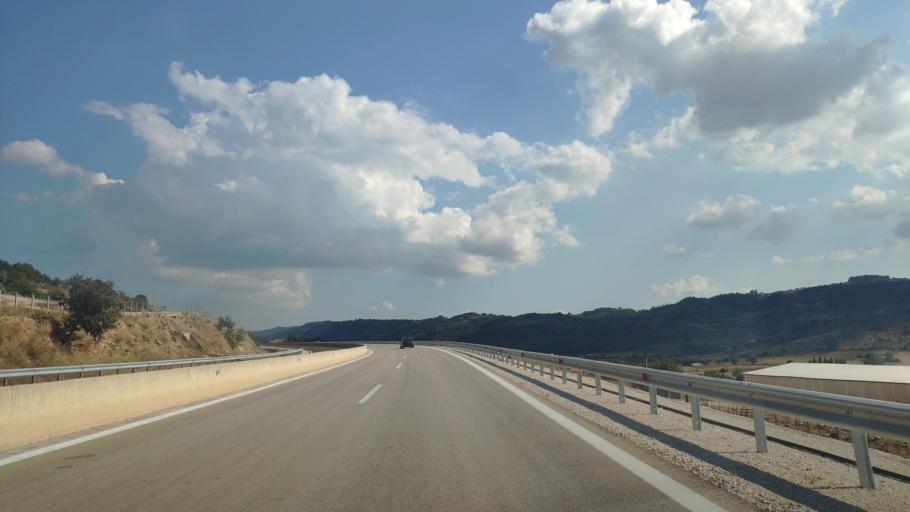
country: GR
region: West Greece
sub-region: Nomos Aitolias kai Akarnanias
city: Katouna
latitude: 38.8117
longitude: 21.1290
